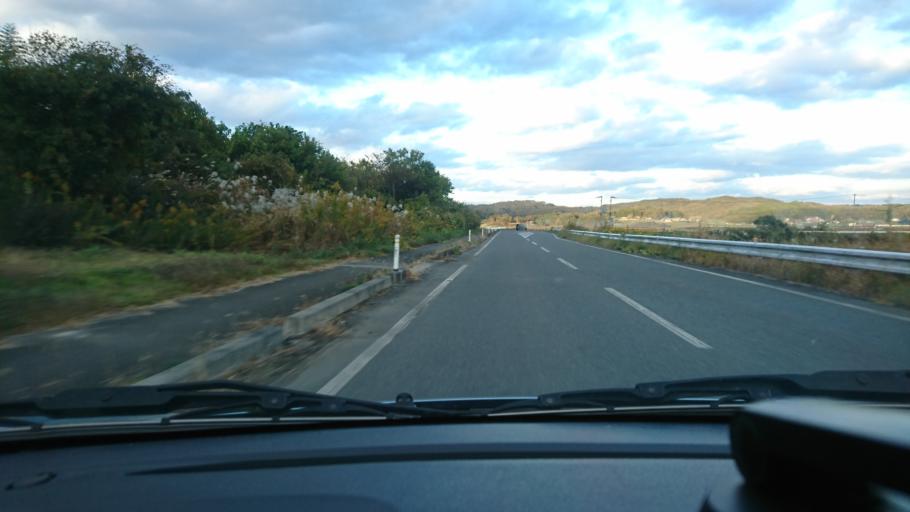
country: JP
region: Iwate
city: Ichinoseki
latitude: 38.8116
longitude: 141.1985
